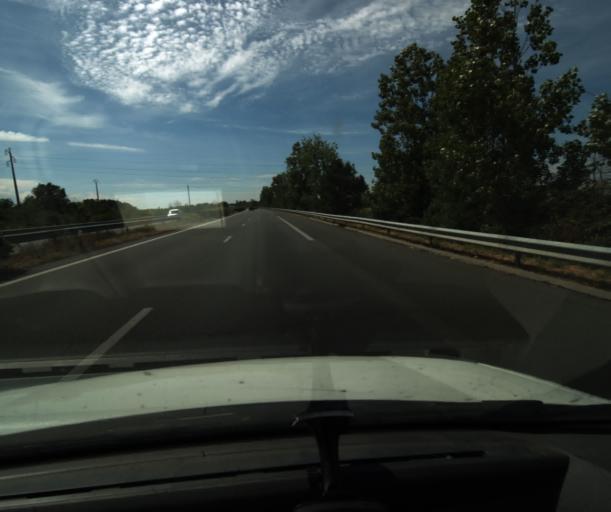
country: FR
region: Midi-Pyrenees
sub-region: Departement du Tarn-et-Garonne
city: Castelsarrasin
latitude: 44.0519
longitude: 1.1340
